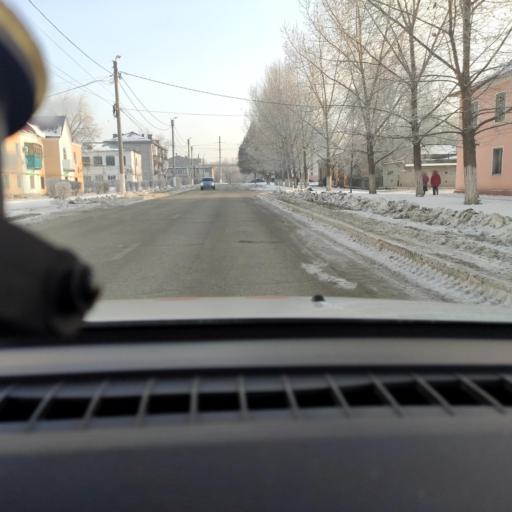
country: RU
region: Samara
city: Chapayevsk
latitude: 52.9726
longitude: 49.7035
